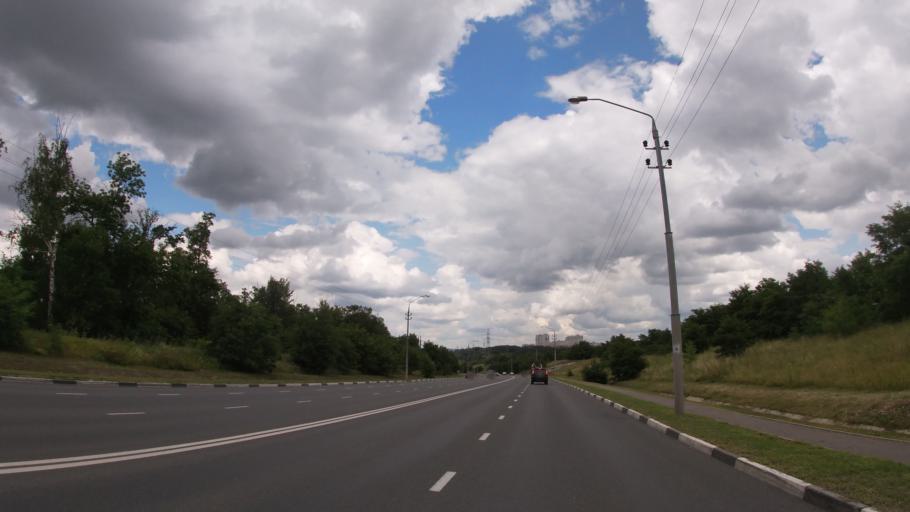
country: RU
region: Belgorod
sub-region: Belgorodskiy Rayon
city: Belgorod
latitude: 50.5546
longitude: 36.5826
